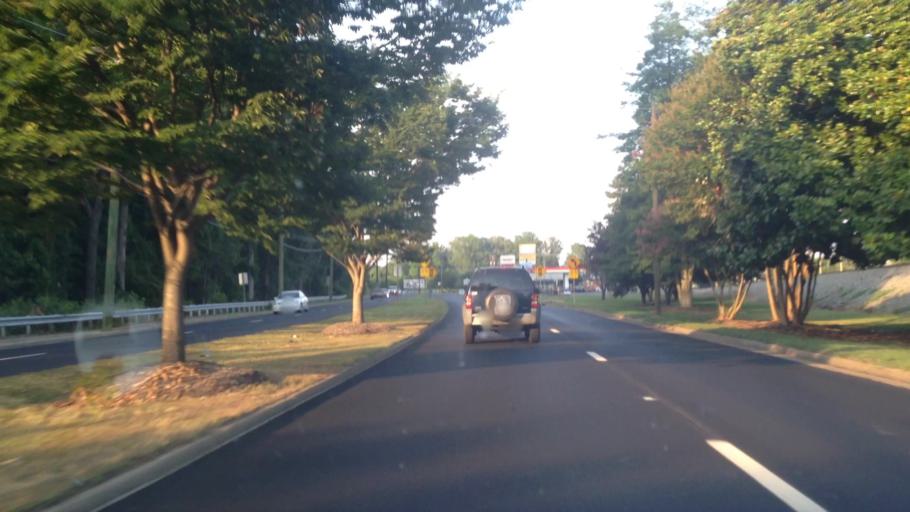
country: US
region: Virginia
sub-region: City of Danville
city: Danville
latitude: 36.5650
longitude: -79.4426
